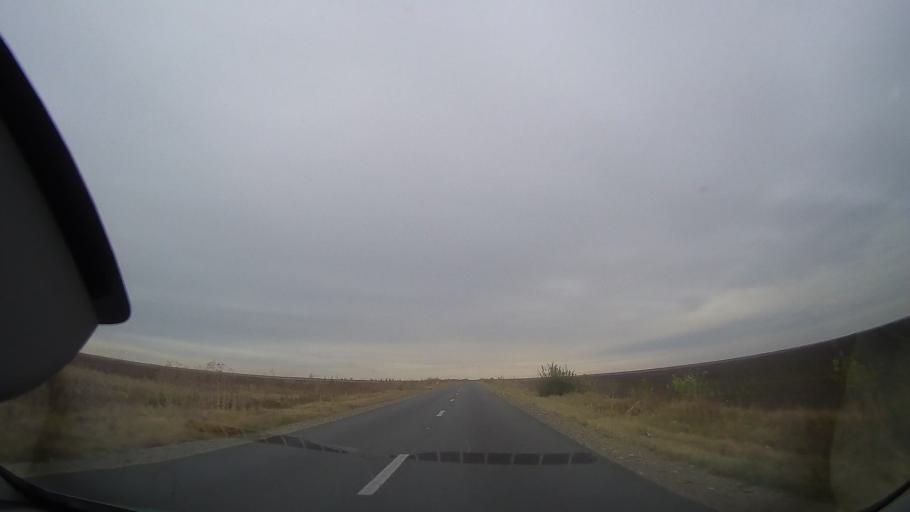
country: RO
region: Ialomita
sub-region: Oras Amara
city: Amara
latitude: 44.6424
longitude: 27.3006
